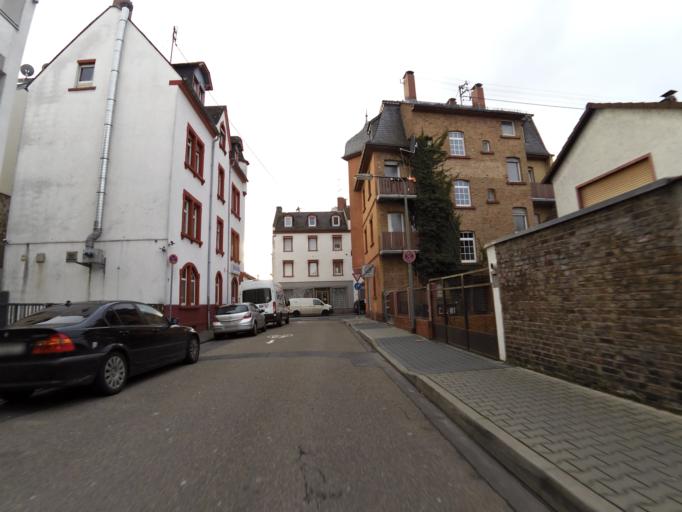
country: DE
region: Hesse
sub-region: Regierungsbezirk Darmstadt
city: Eschborn
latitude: 50.0989
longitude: 8.5670
